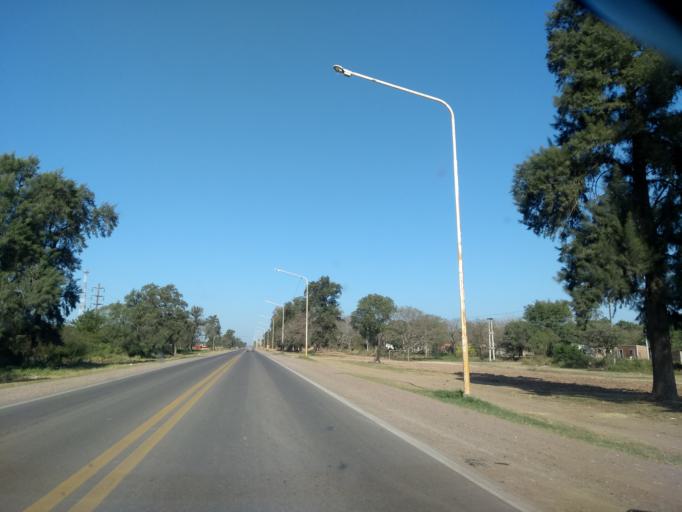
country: AR
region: Chaco
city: Presidencia Roque Saenz Pena
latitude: -26.7922
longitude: -60.4095
